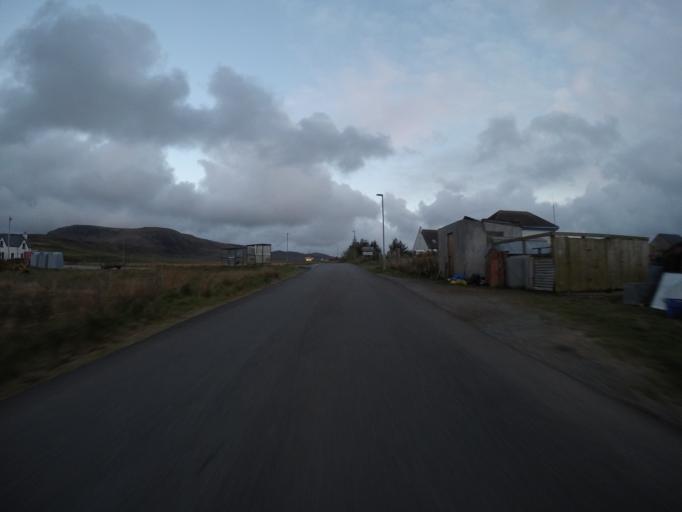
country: GB
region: Scotland
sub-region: Highland
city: Portree
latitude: 57.6476
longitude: -6.3800
